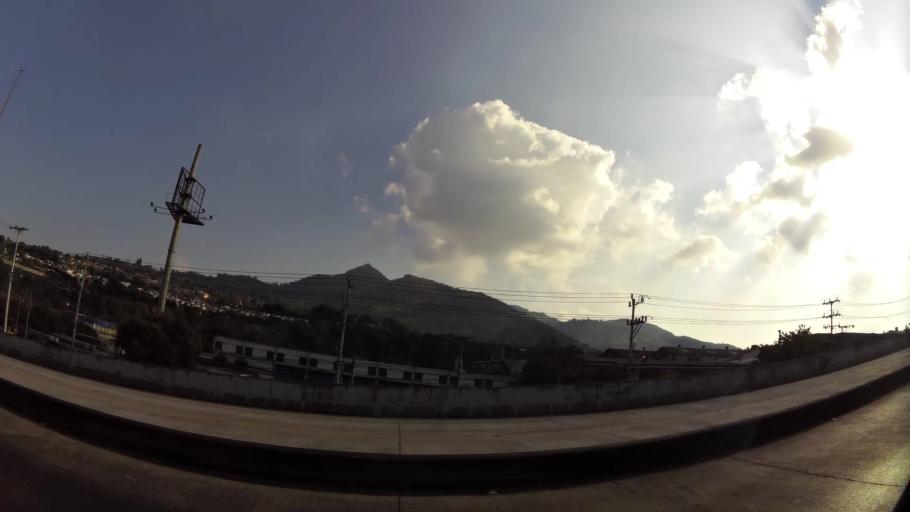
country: SV
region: San Salvador
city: San Salvador
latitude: 13.7007
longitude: -89.1679
